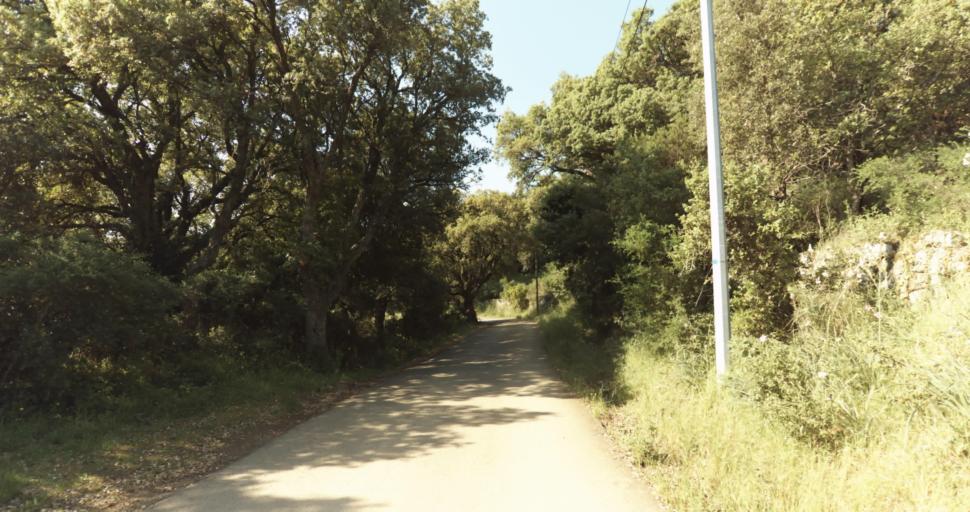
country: FR
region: Corsica
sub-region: Departement de la Haute-Corse
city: Furiani
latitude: 42.6389
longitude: 9.4163
